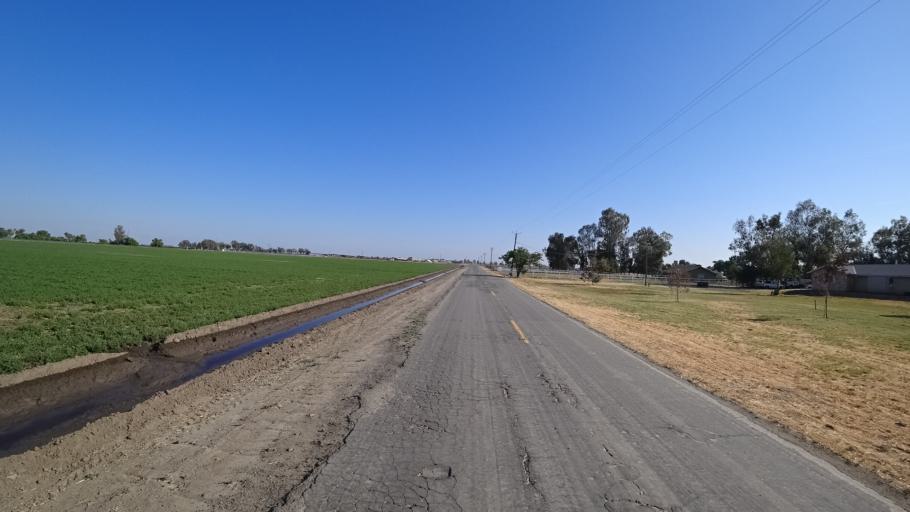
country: US
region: California
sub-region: Kings County
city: Lemoore Station
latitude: 36.3325
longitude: -119.8783
